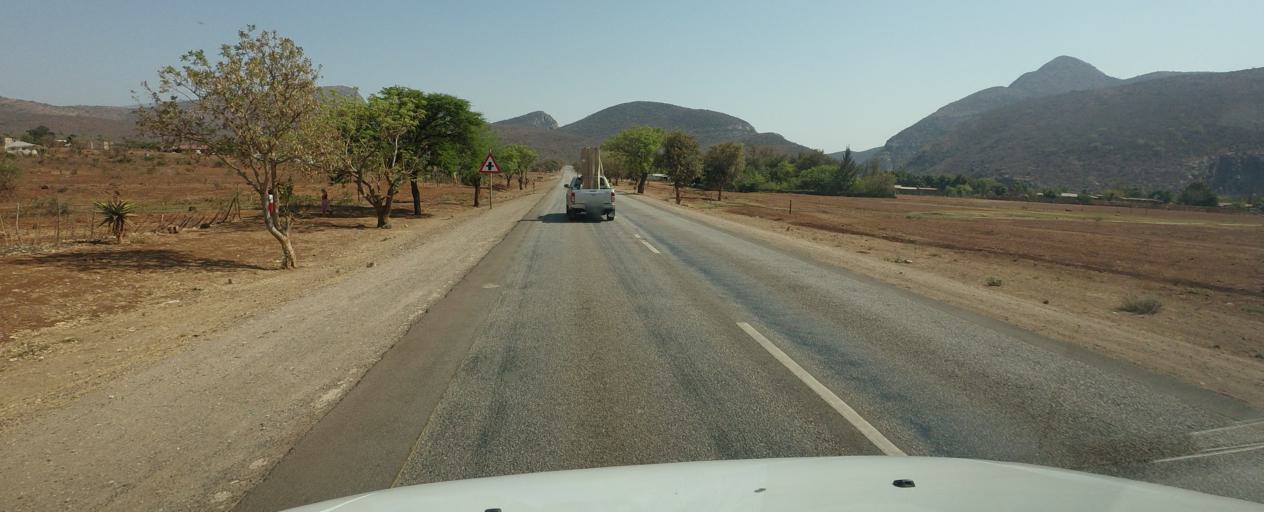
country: ZA
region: Mpumalanga
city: Burgersfort
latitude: -24.4761
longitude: 30.6065
